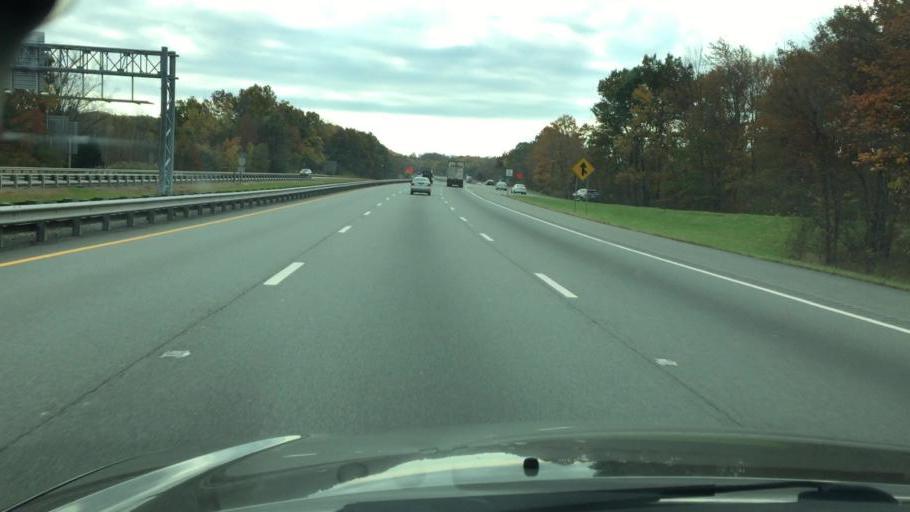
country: US
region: New Jersey
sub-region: Sussex County
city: Stanhope
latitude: 40.9014
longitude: -74.7207
